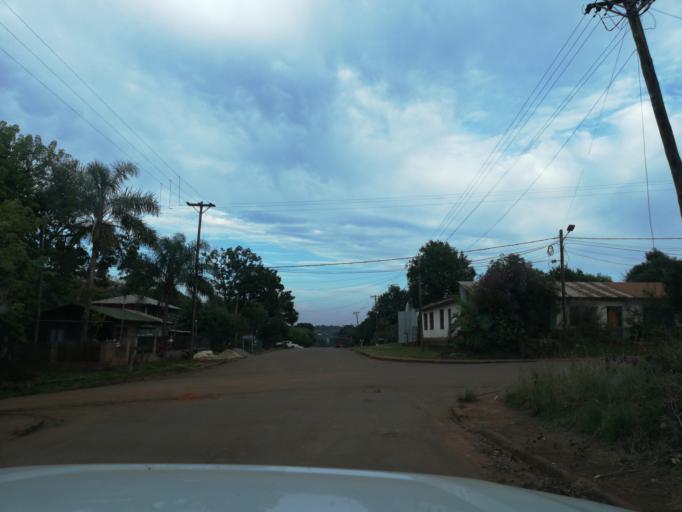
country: AR
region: Misiones
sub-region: Departamento de San Pedro
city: San Pedro
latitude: -26.6265
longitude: -54.1023
